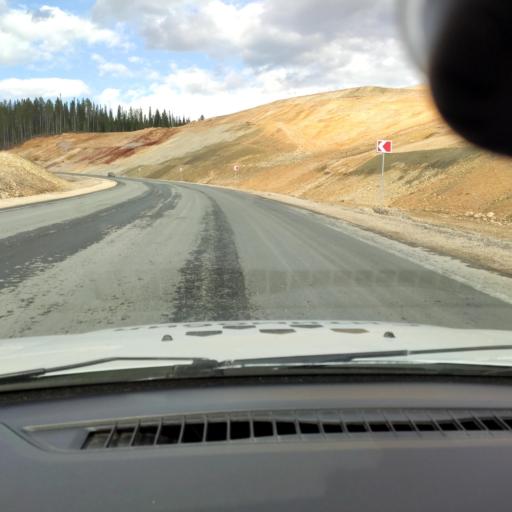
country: RU
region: Perm
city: Chusovoy
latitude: 58.3305
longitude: 57.7920
